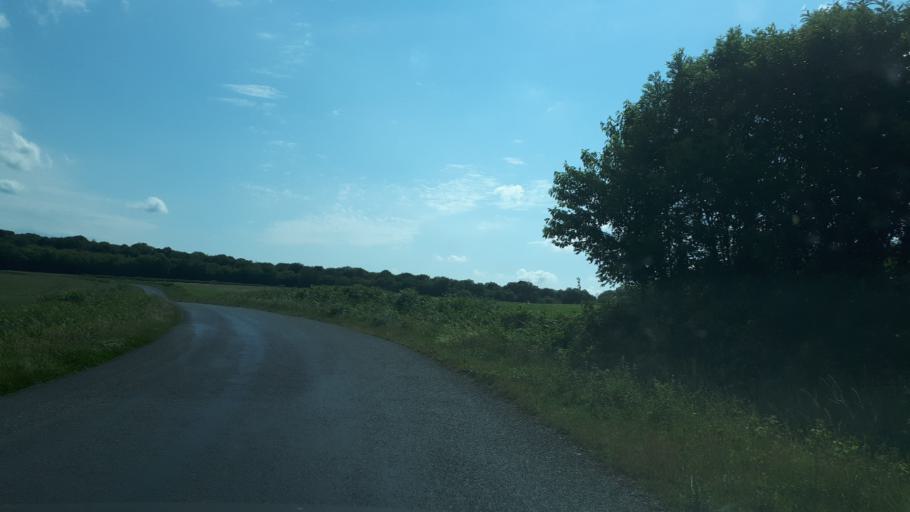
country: FR
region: Centre
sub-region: Departement du Cher
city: Henrichemont
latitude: 47.4014
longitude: 2.5968
